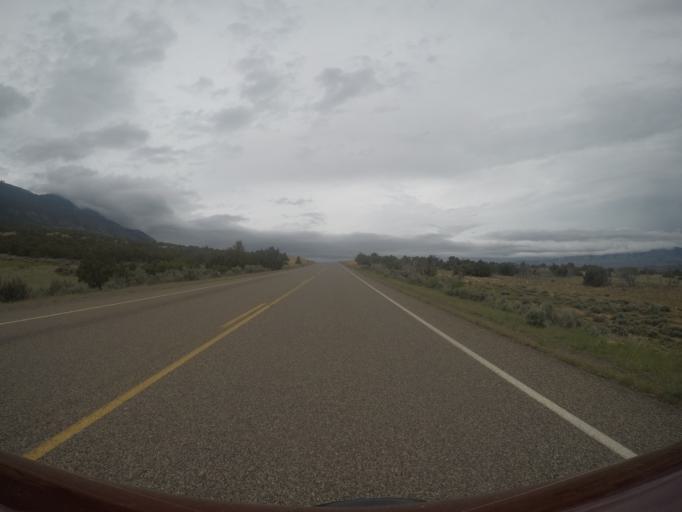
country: US
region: Wyoming
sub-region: Big Horn County
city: Lovell
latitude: 45.0910
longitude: -108.2507
